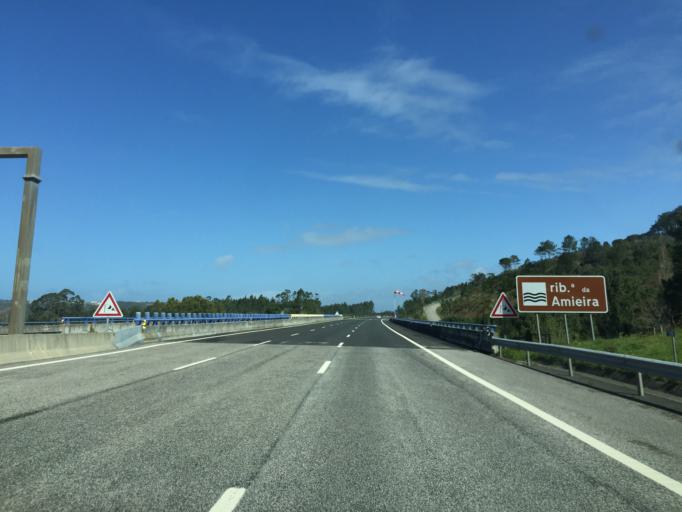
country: PT
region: Leiria
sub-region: Nazare
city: Nazare
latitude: 39.5137
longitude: -9.0880
